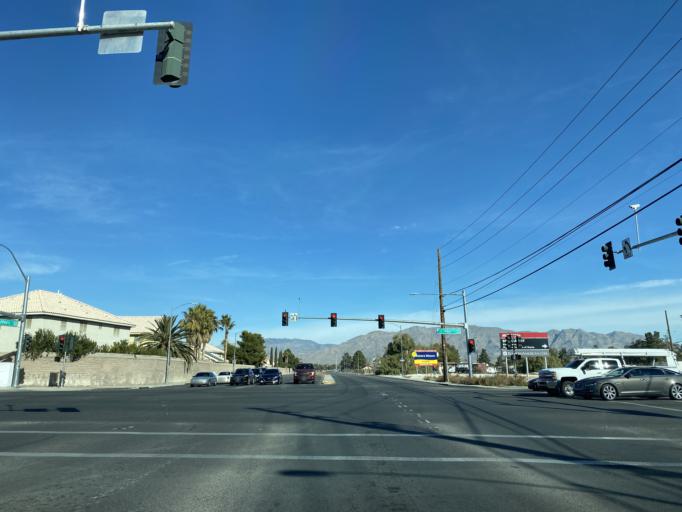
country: US
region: Nevada
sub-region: Clark County
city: Las Vegas
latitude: 36.2609
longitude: -115.2254
